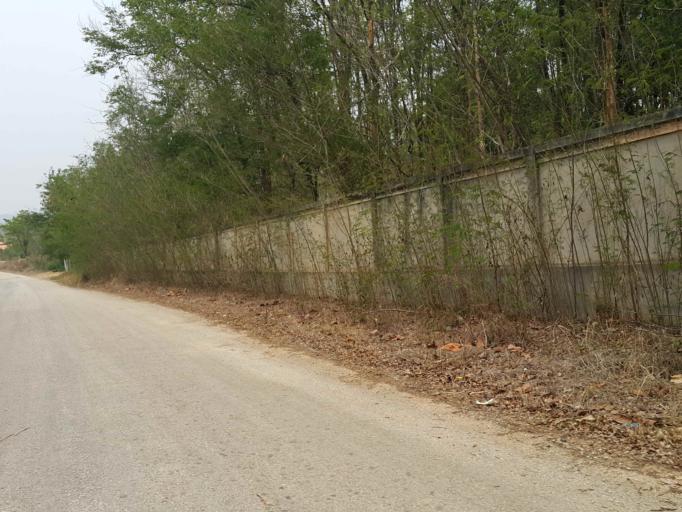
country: TH
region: Chiang Mai
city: San Sai
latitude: 18.9334
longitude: 99.0129
